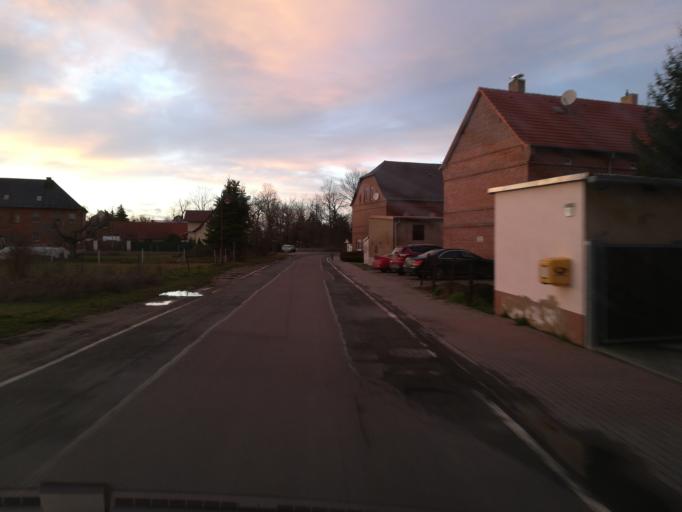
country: DE
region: Saxony-Anhalt
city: Brehna
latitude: 51.5265
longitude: 12.2284
